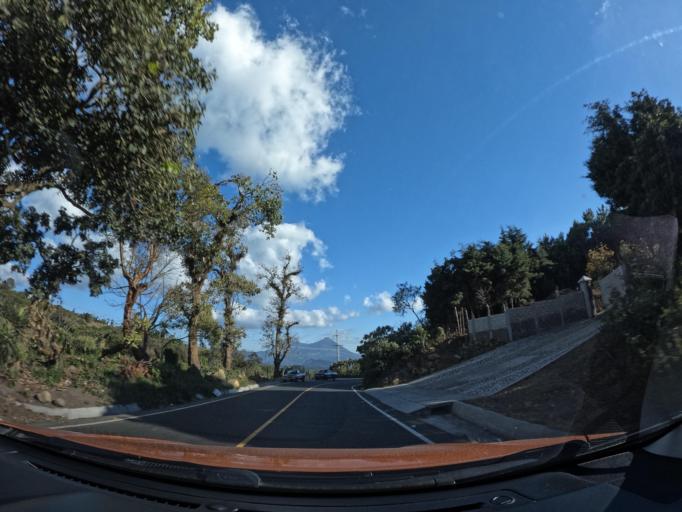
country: GT
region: Sacatepequez
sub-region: Municipio de Santa Maria de Jesus
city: Santa Maria de Jesus
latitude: 14.4710
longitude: -90.6922
